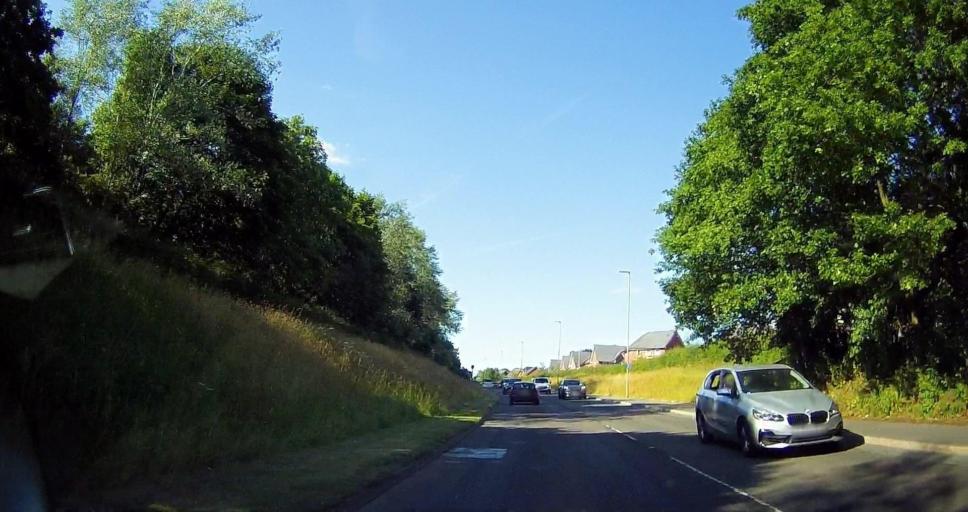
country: GB
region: England
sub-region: Cheshire East
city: Sandbach
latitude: 53.1474
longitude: -2.3525
